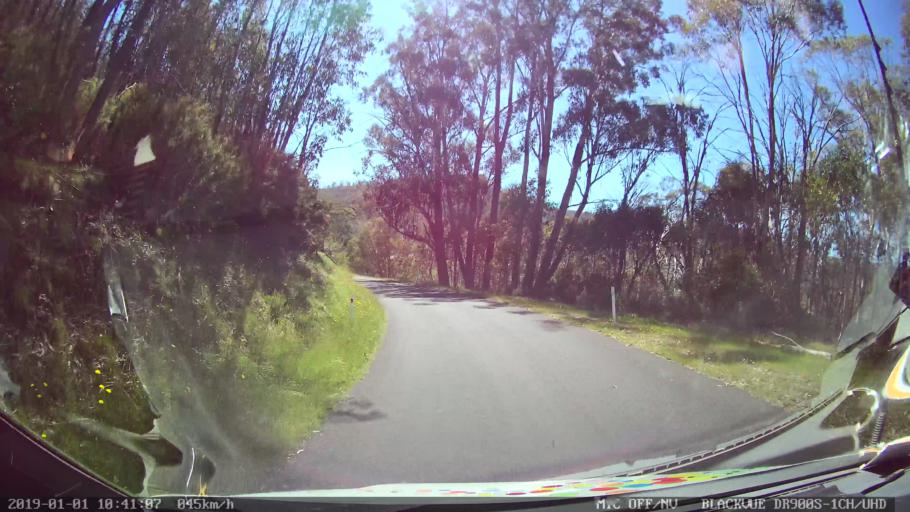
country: AU
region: New South Wales
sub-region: Snowy River
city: Jindabyne
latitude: -36.0369
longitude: 148.3177
